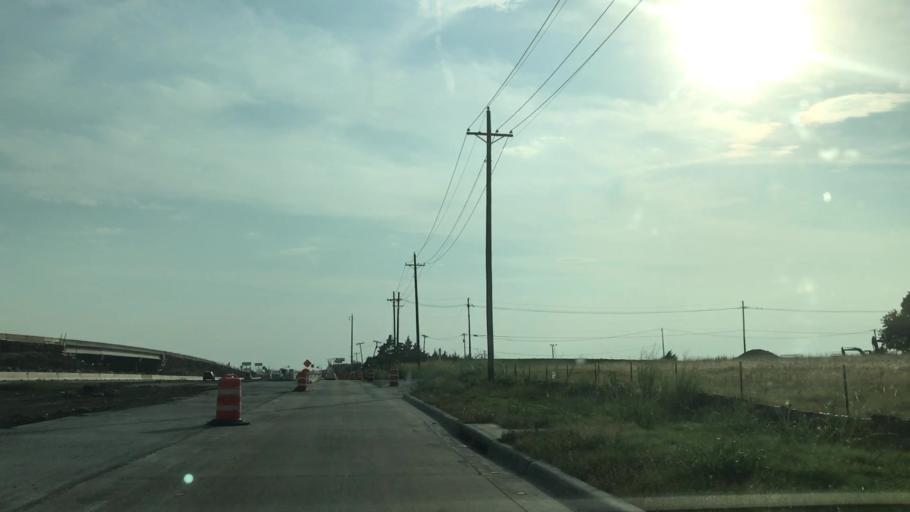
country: US
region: Texas
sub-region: Rockwall County
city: Fate
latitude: 32.9205
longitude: -96.4162
